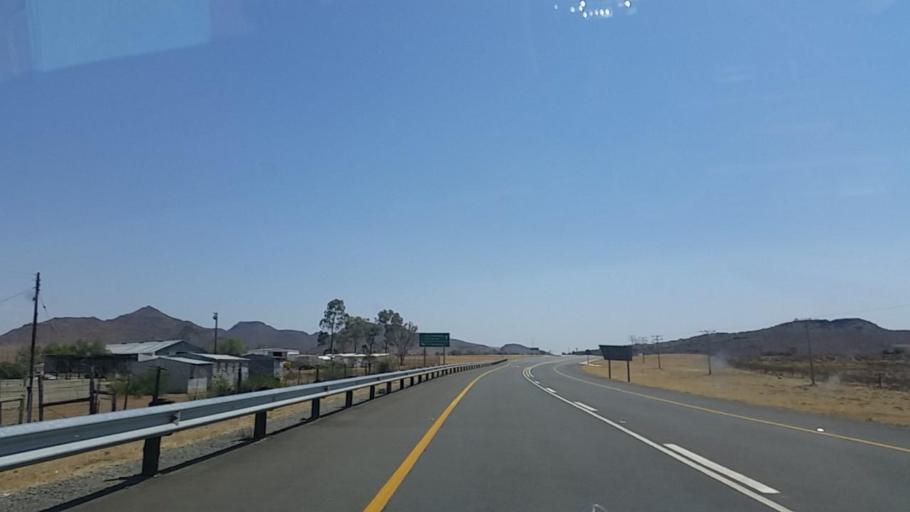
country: ZA
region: Eastern Cape
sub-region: Chris Hani District Municipality
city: Middelburg
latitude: -31.4852
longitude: 25.0110
